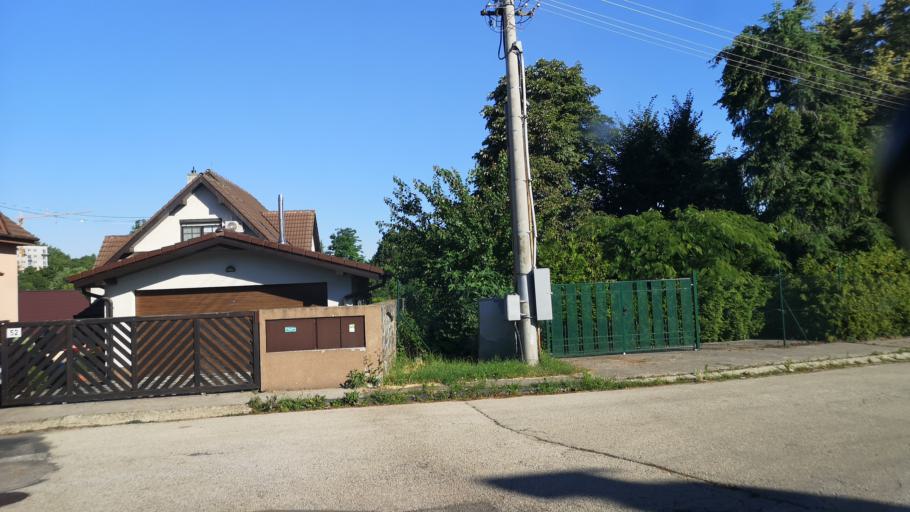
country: SK
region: Nitriansky
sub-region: Okres Nitra
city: Nitra
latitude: 48.3084
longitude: 18.0566
